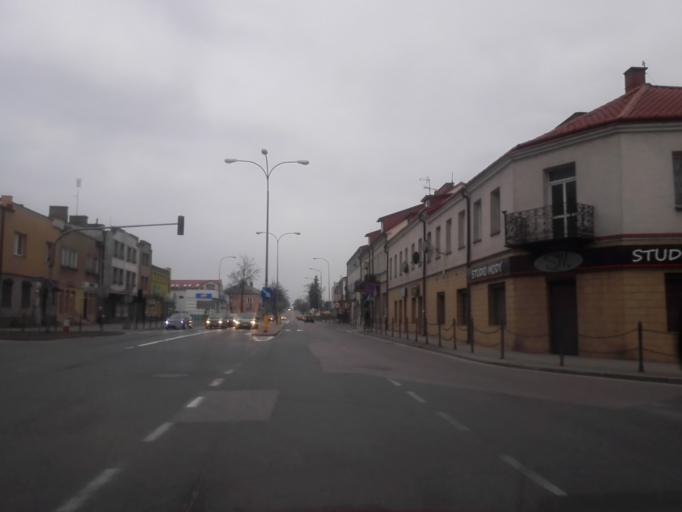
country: PL
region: Podlasie
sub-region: Powiat grajewski
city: Grajewo
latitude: 53.6471
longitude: 22.4550
